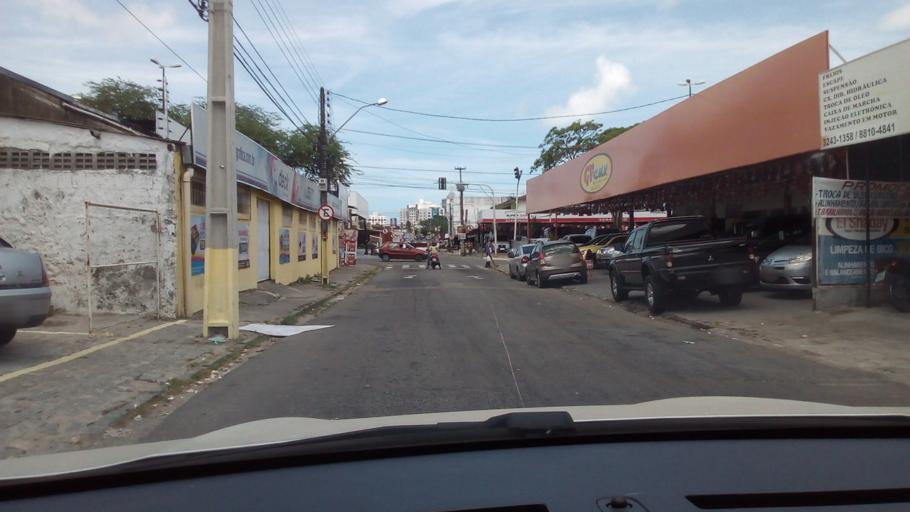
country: BR
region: Paraiba
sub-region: Joao Pessoa
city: Joao Pessoa
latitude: -7.1272
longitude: -34.8635
